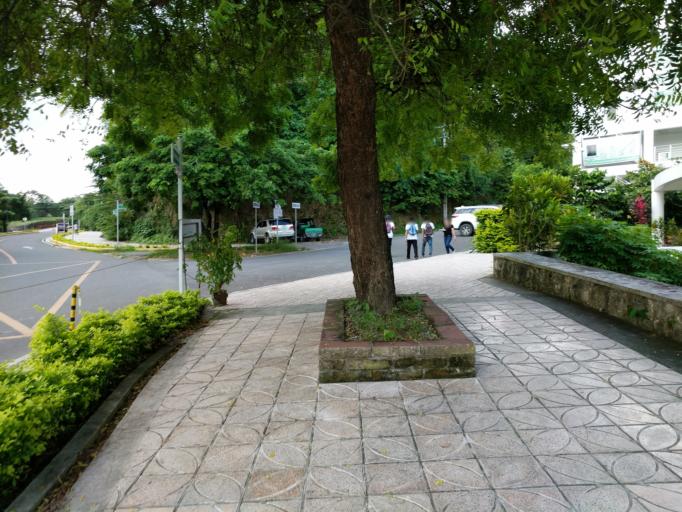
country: PH
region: Central Visayas
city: Mandaue City
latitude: 10.3554
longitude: 123.9106
